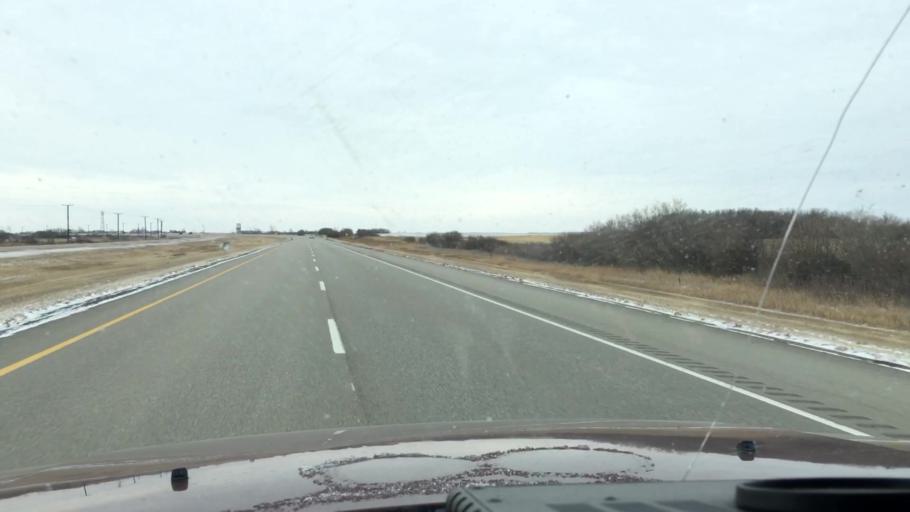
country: CA
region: Saskatchewan
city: Watrous
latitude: 51.3848
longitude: -106.1628
